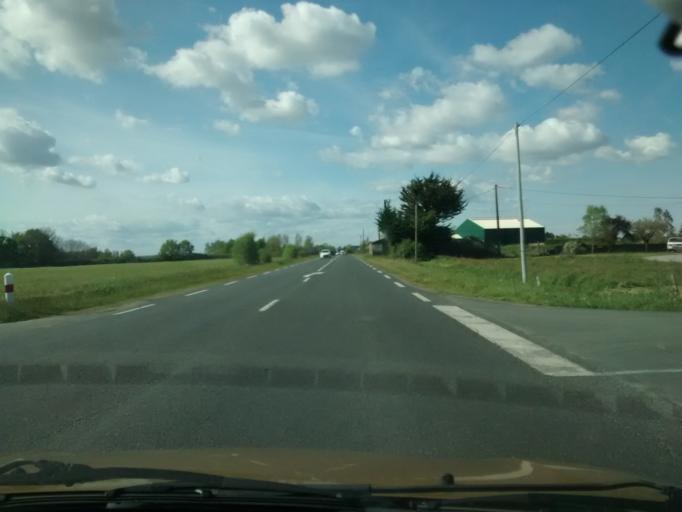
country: FR
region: Pays de la Loire
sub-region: Departement de la Loire-Atlantique
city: Les Sorinieres
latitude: 47.1060
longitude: -1.5368
